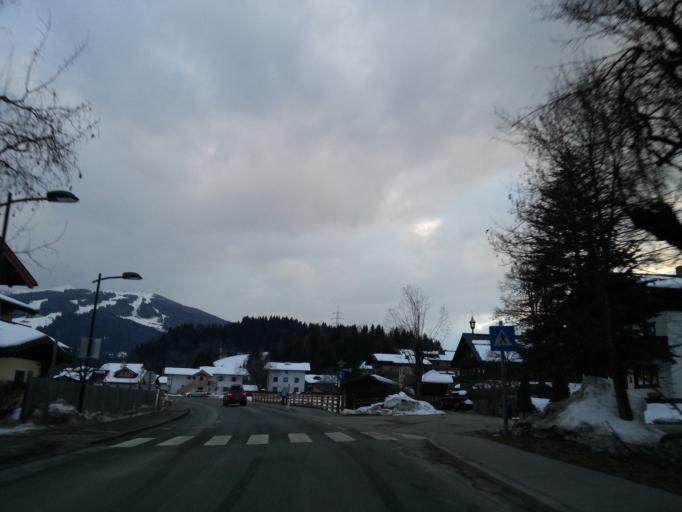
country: AT
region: Salzburg
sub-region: Politischer Bezirk Sankt Johann im Pongau
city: Flachau
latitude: 47.3722
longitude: 13.3883
